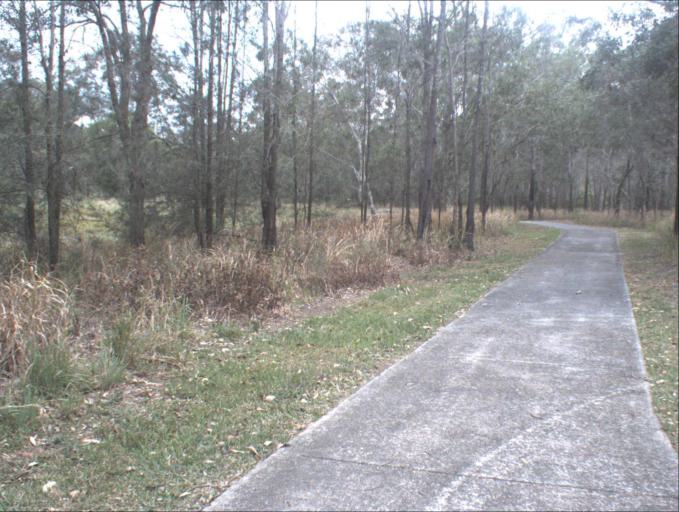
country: AU
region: Queensland
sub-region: Logan
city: Slacks Creek
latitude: -27.6494
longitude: 153.1400
